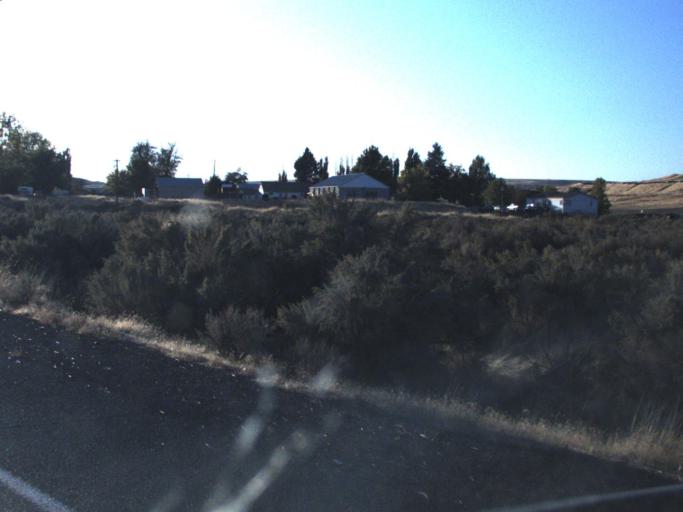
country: US
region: Washington
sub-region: Franklin County
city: Connell
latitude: 46.6441
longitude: -118.5547
